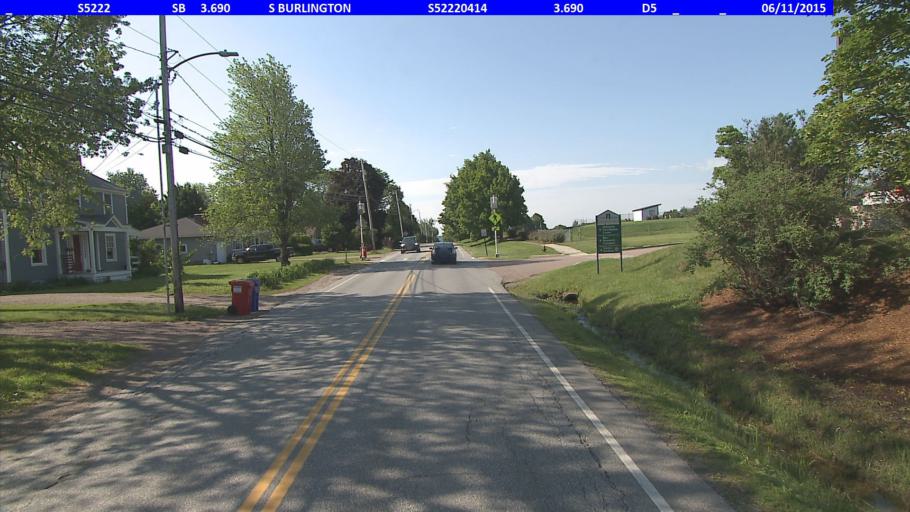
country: US
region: Vermont
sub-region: Chittenden County
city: Burlington
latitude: 44.4695
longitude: -73.1920
